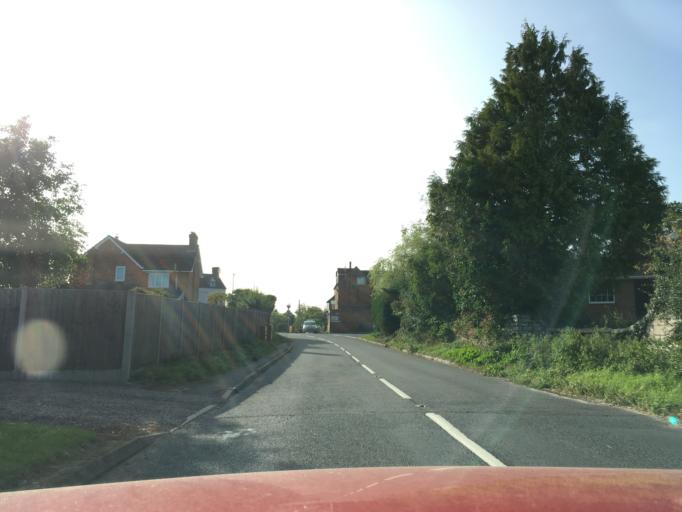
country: GB
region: England
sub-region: Gloucestershire
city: Newent
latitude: 51.9627
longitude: -2.3027
